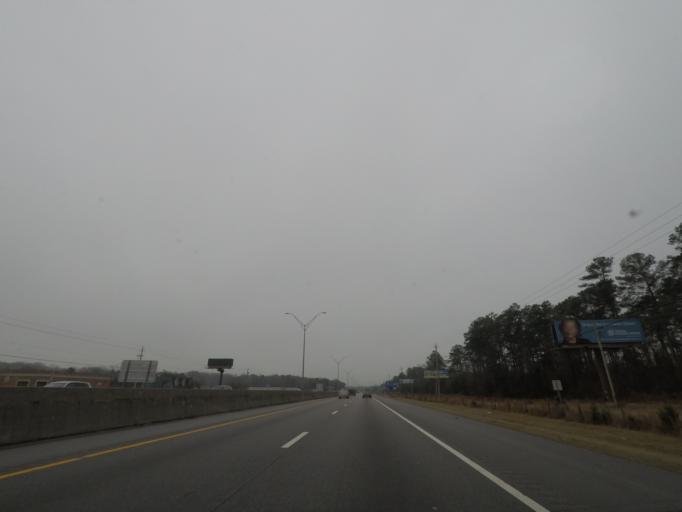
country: US
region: North Carolina
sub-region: Robeson County
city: Lumberton
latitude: 34.6587
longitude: -79.0097
